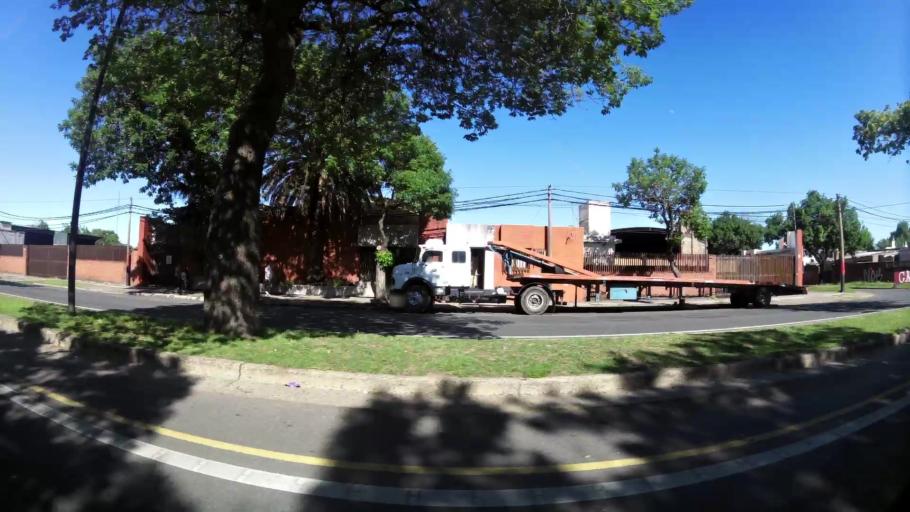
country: AR
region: Santa Fe
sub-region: Departamento de Rosario
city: Rosario
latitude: -32.9618
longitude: -60.6707
